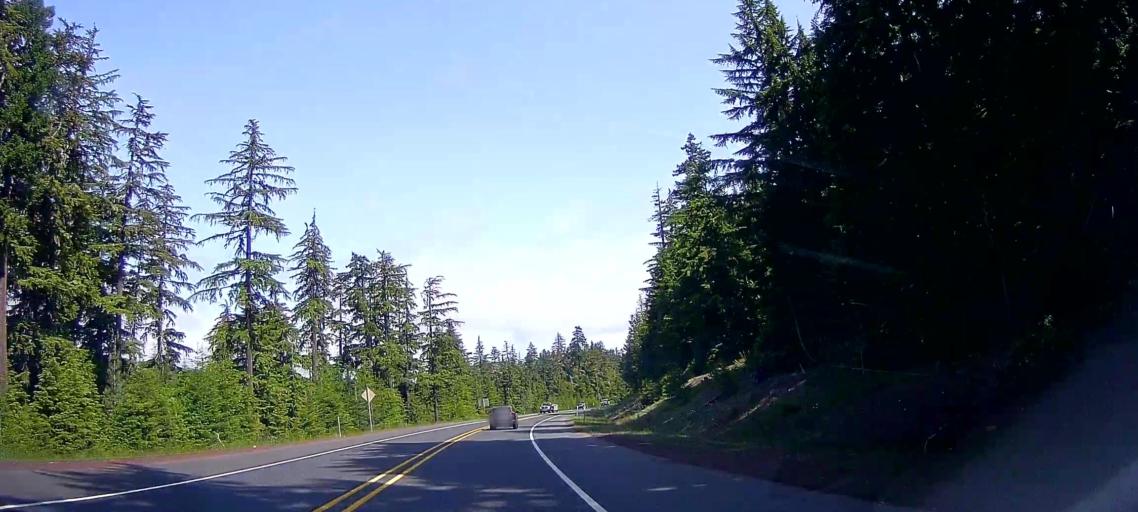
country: US
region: Oregon
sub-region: Clackamas County
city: Mount Hood Village
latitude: 45.1966
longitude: -121.6918
